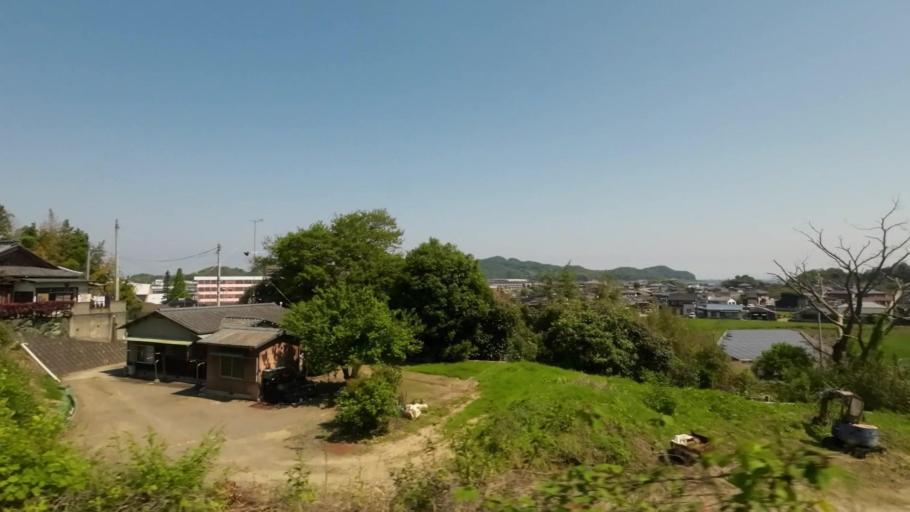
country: JP
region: Ehime
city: Niihama
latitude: 33.9722
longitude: 133.3524
